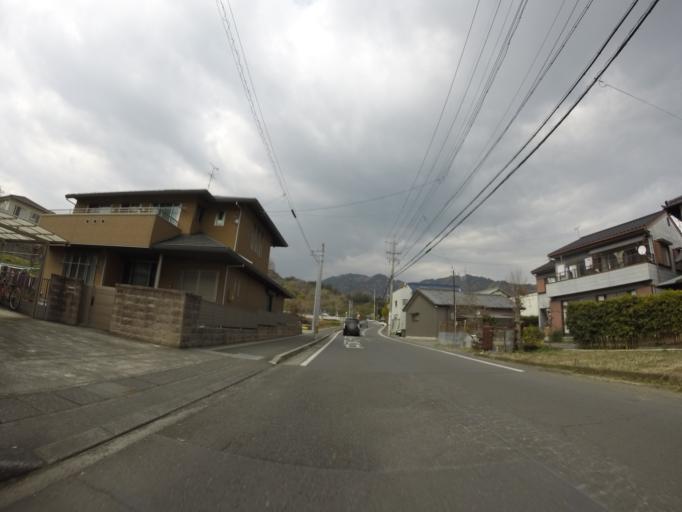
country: JP
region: Shizuoka
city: Shizuoka-shi
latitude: 35.0379
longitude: 138.4491
